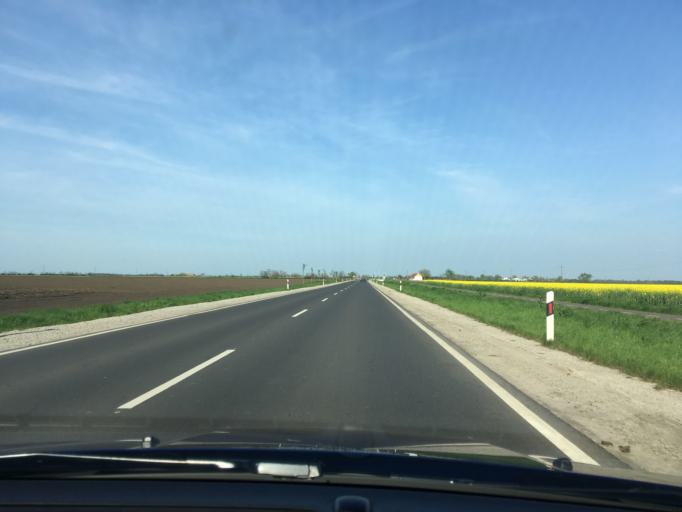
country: HU
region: Bekes
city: Csorvas
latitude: 46.6468
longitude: 20.8994
